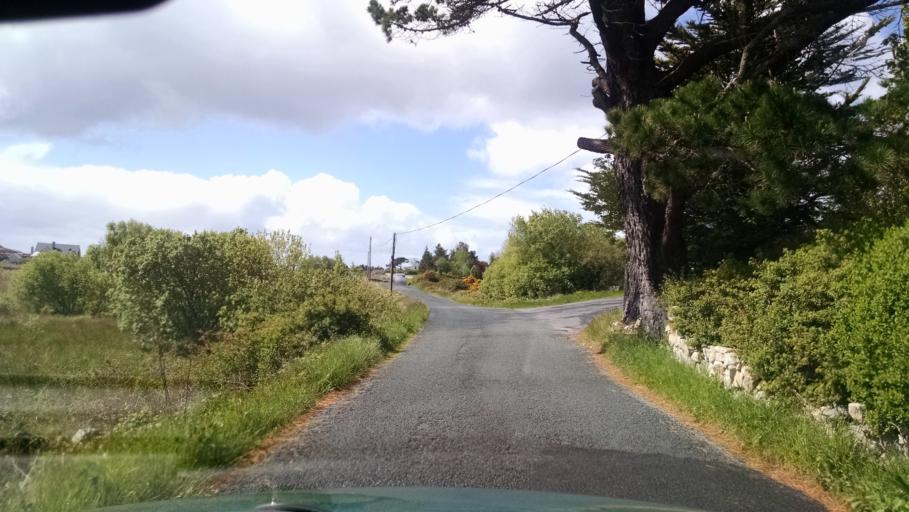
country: IE
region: Connaught
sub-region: County Galway
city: Oughterard
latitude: 53.2552
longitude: -9.6139
